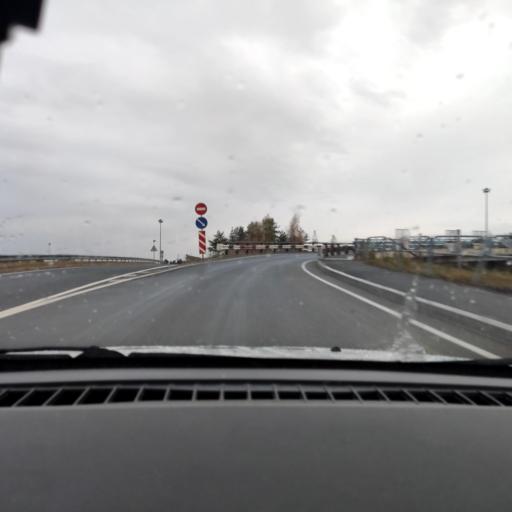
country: RU
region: Perm
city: Kondratovo
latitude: 58.0402
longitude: 56.0452
